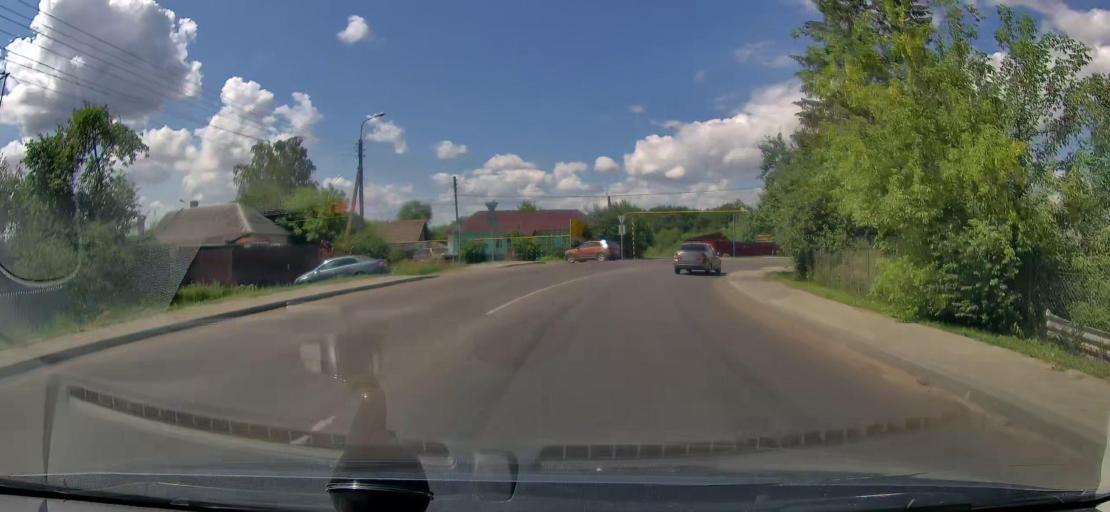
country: RU
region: Kursk
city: Zolotukhino
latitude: 51.9724
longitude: 36.2976
